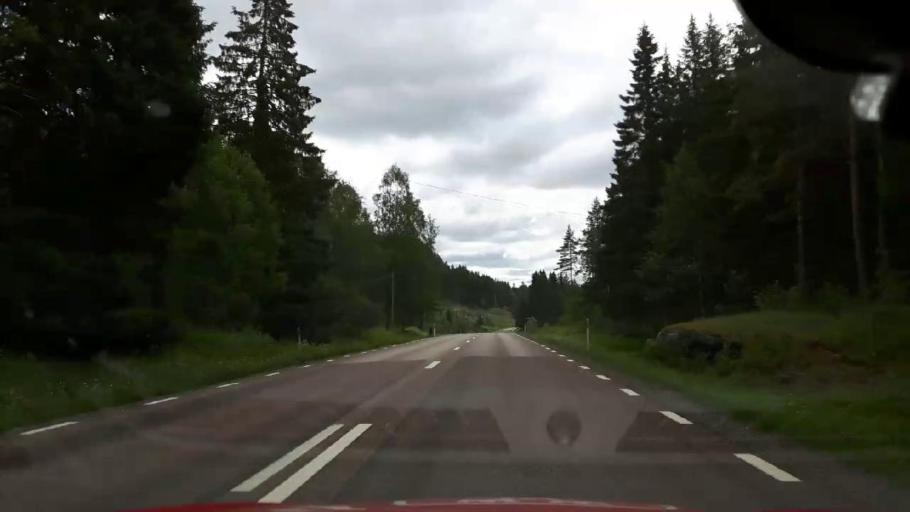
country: SE
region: Jaemtland
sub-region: OEstersunds Kommun
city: Brunflo
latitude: 62.9761
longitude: 15.0108
